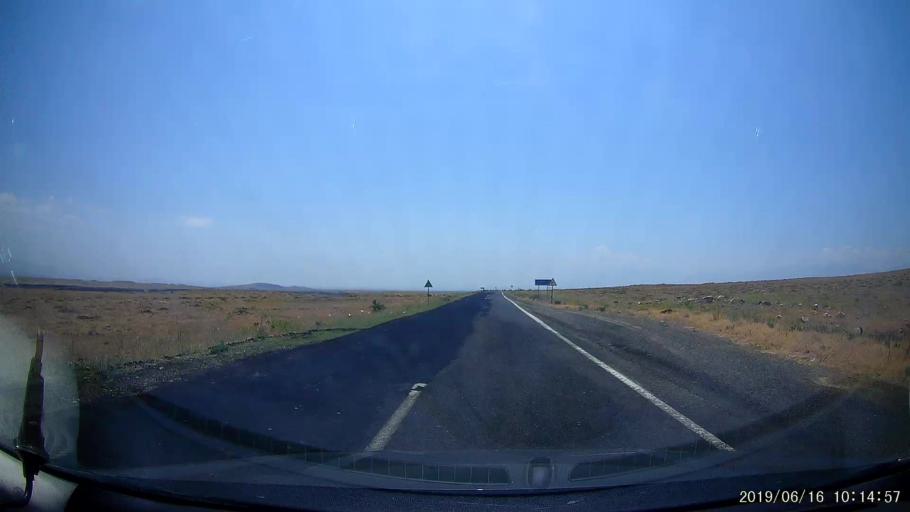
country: TR
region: Igdir
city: Tuzluca
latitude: 40.1804
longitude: 43.6733
